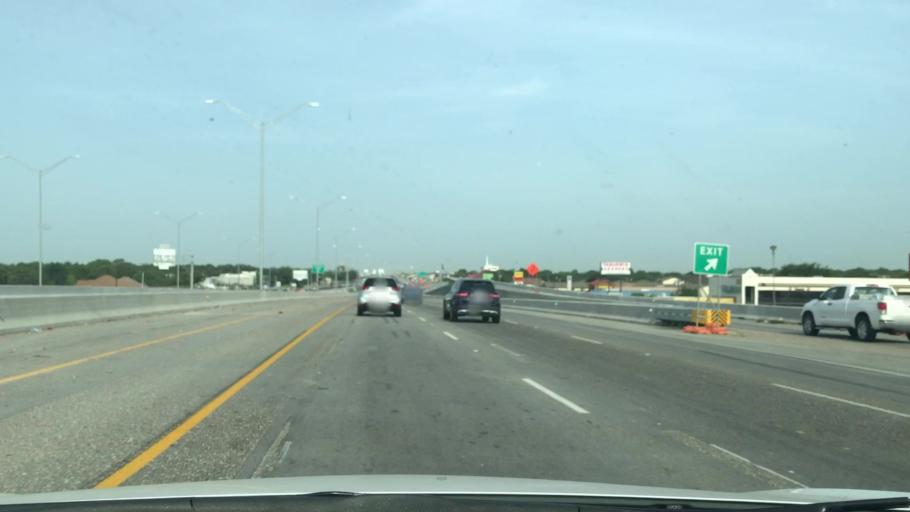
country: US
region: Texas
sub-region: Dallas County
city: Irving
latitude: 32.8375
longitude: -96.9556
